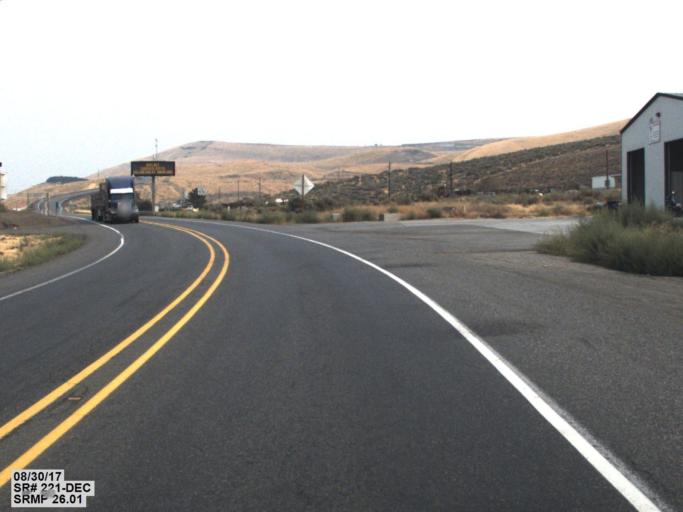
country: US
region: Washington
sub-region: Benton County
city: Prosser
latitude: 46.2060
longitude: -119.7474
